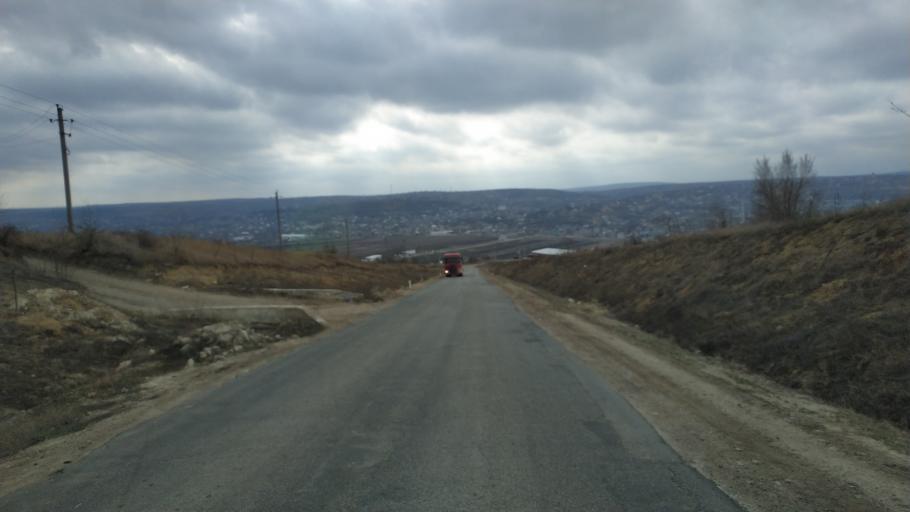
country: MD
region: Laloveni
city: Ialoveni
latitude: 46.8863
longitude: 28.7674
